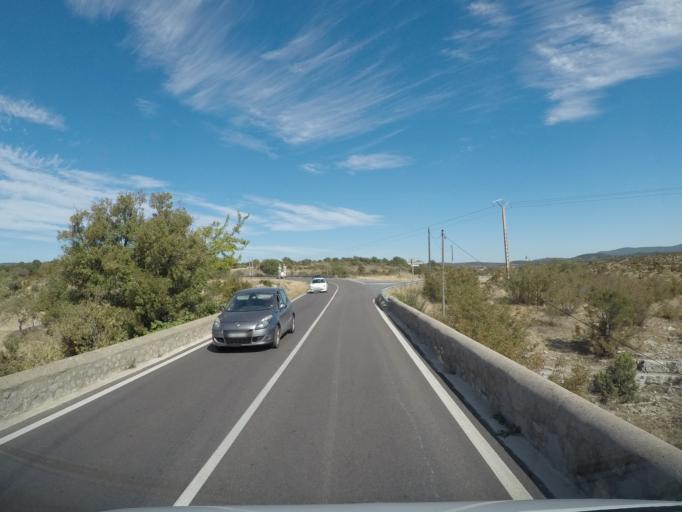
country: FR
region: Languedoc-Roussillon
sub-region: Departement de l'Herault
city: Saint-Martin-de-Londres
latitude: 43.8122
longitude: 3.7427
